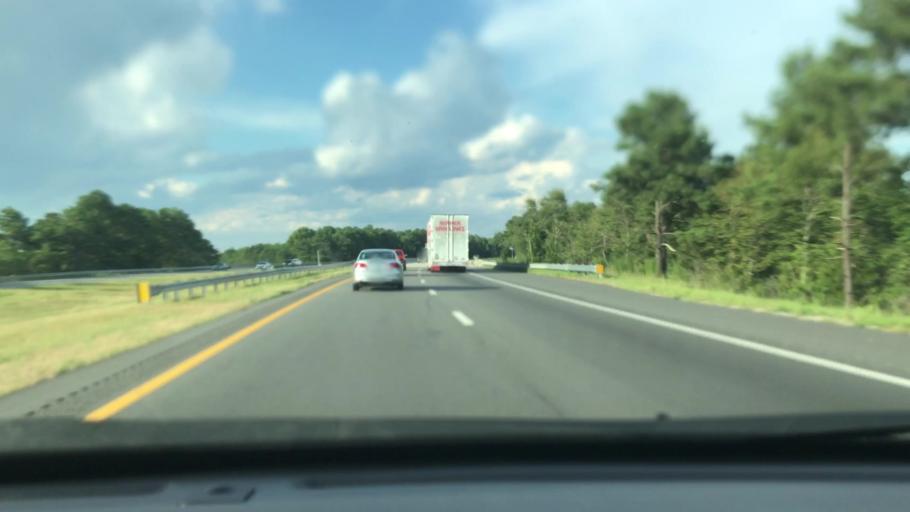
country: US
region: North Carolina
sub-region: Cumberland County
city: Hope Mills
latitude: 34.9298
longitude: -78.9394
